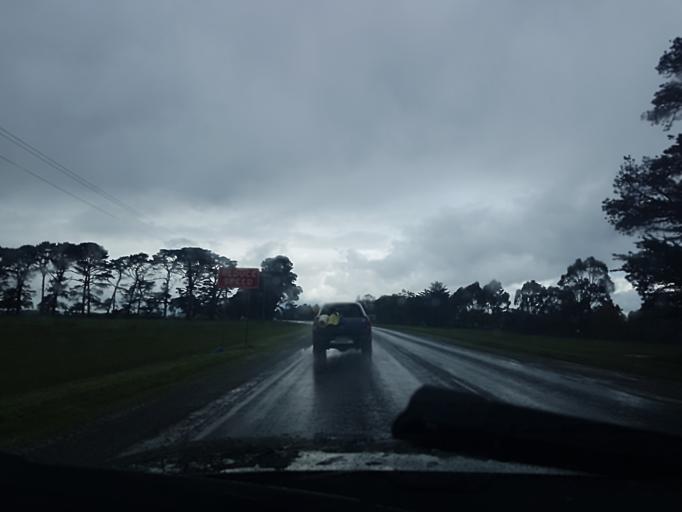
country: AU
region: Victoria
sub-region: Ballarat North
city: Newington
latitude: -37.5391
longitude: 143.8012
